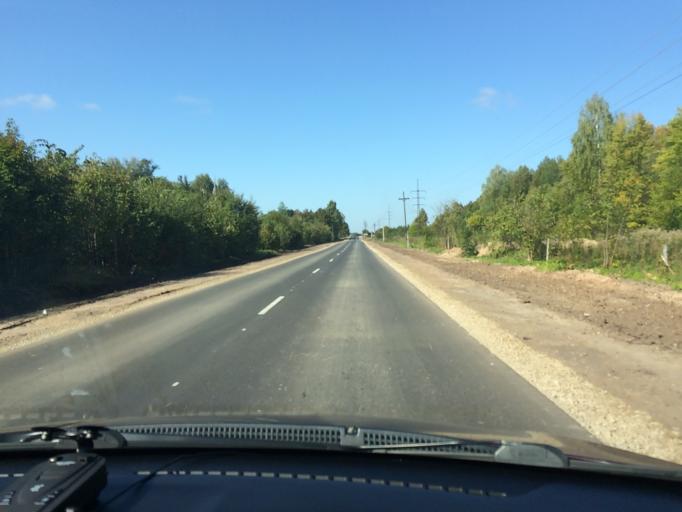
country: RU
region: Mariy-El
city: Sovetskiy
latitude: 56.5460
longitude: 48.4186
